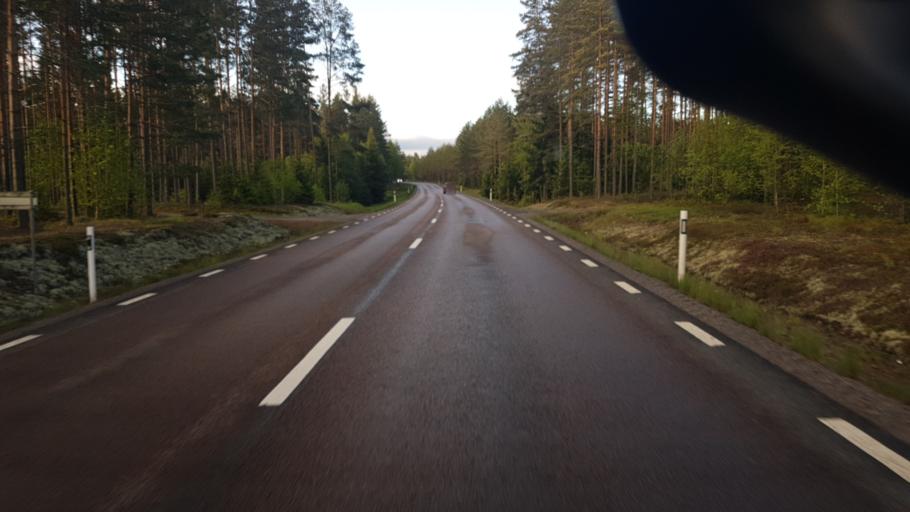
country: SE
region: Vaermland
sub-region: Eda Kommun
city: Charlottenberg
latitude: 59.9094
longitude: 12.2750
